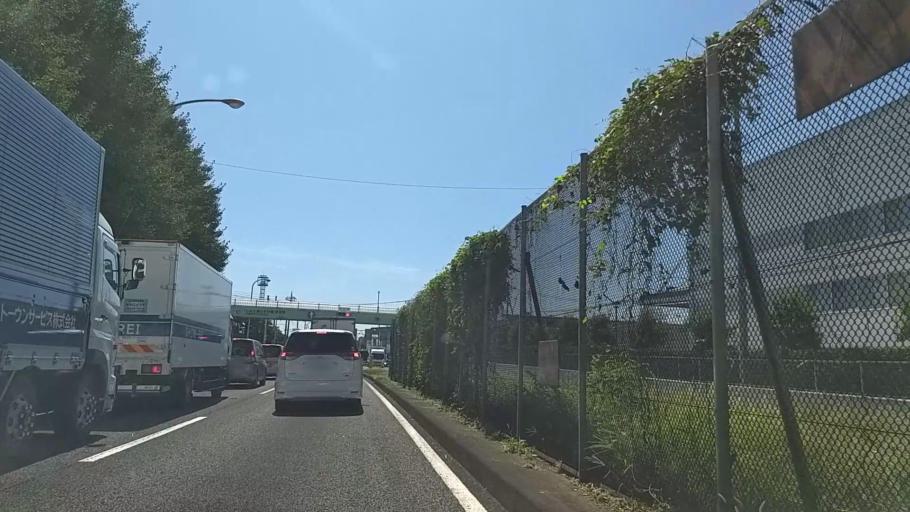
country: JP
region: Kanagawa
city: Zama
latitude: 35.5373
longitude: 139.3616
